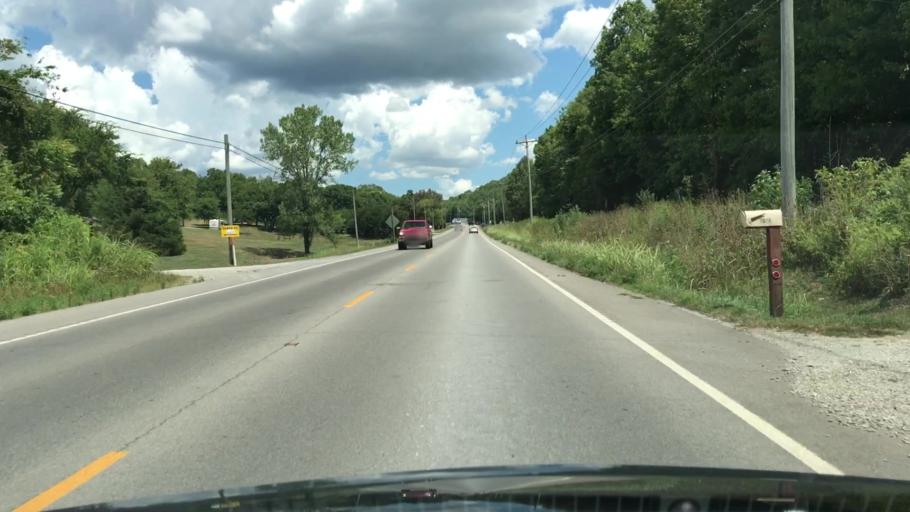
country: US
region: Tennessee
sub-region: Williamson County
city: Nolensville
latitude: 35.9148
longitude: -86.6599
